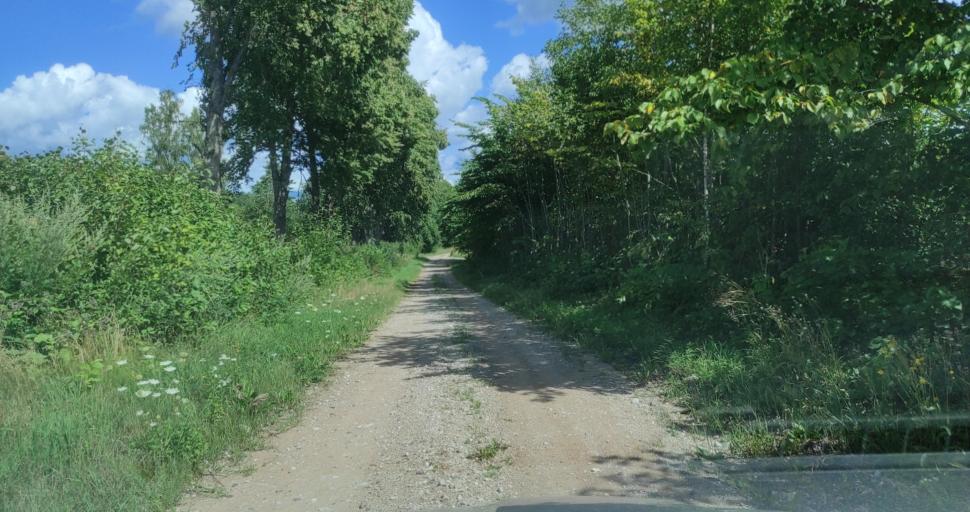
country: LV
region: Alsunga
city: Alsunga
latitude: 57.0284
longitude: 21.6986
